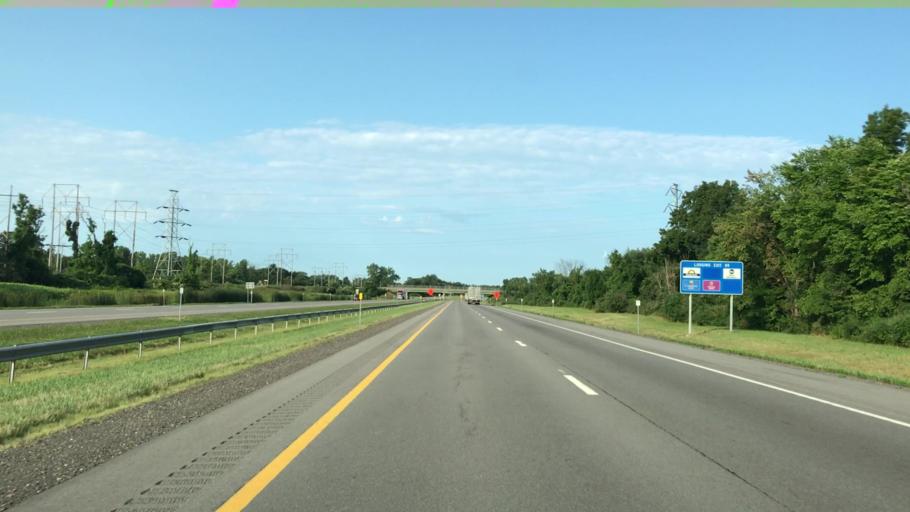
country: US
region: New York
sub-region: Chautauqua County
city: Dunkirk
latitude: 42.4680
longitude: -79.2894
